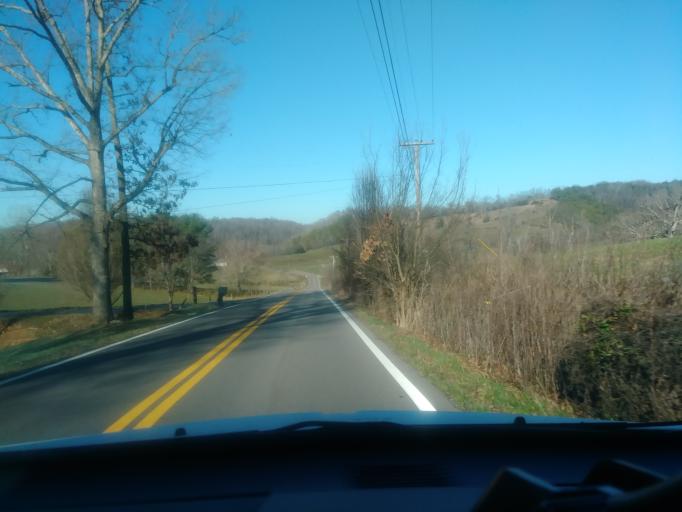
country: US
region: Tennessee
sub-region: Greene County
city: Mosheim
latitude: 36.1179
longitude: -82.9925
